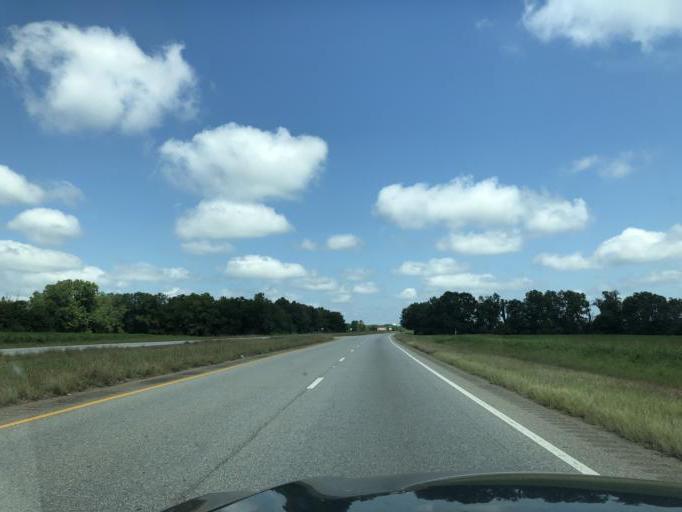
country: US
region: Alabama
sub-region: Henry County
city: Abbeville
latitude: 31.5299
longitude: -85.2911
